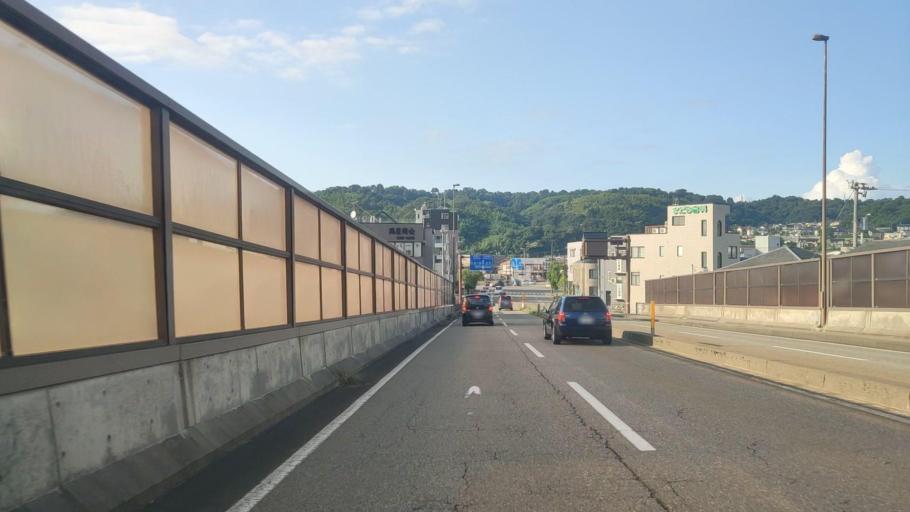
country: JP
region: Ishikawa
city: Kanazawa-shi
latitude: 36.5590
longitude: 136.6770
